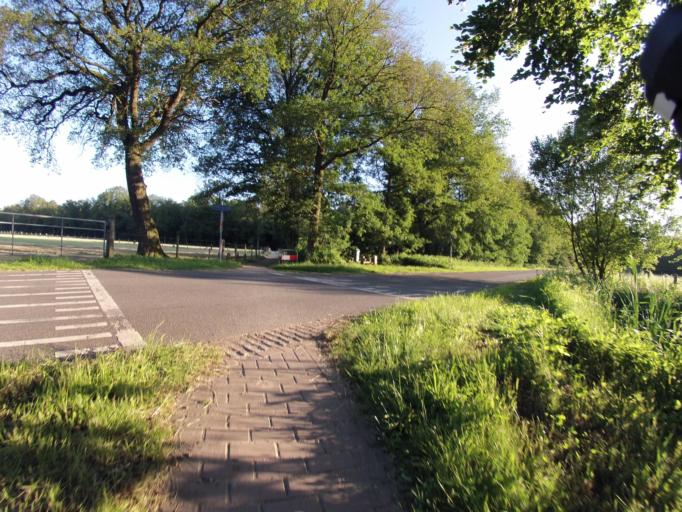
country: NL
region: Overijssel
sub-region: Gemeente Oldenzaal
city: Oldenzaal
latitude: 52.2983
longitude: 6.9701
